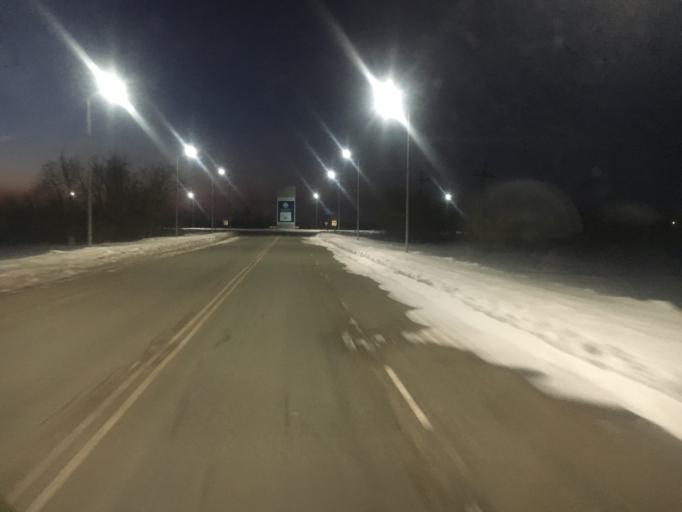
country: KZ
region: Batys Qazaqstan
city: Oral
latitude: 51.1643
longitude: 51.5252
